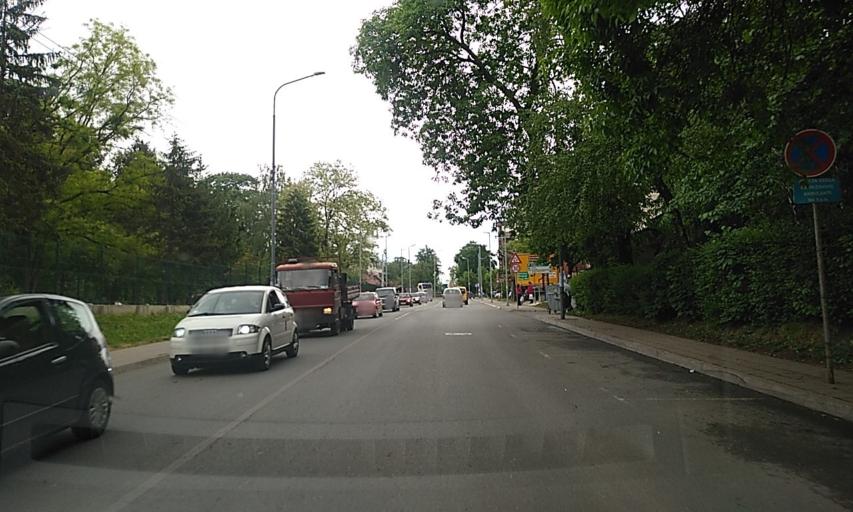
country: RS
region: Central Serbia
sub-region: Rasinski Okrug
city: Krusevac
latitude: 43.5849
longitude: 21.3311
